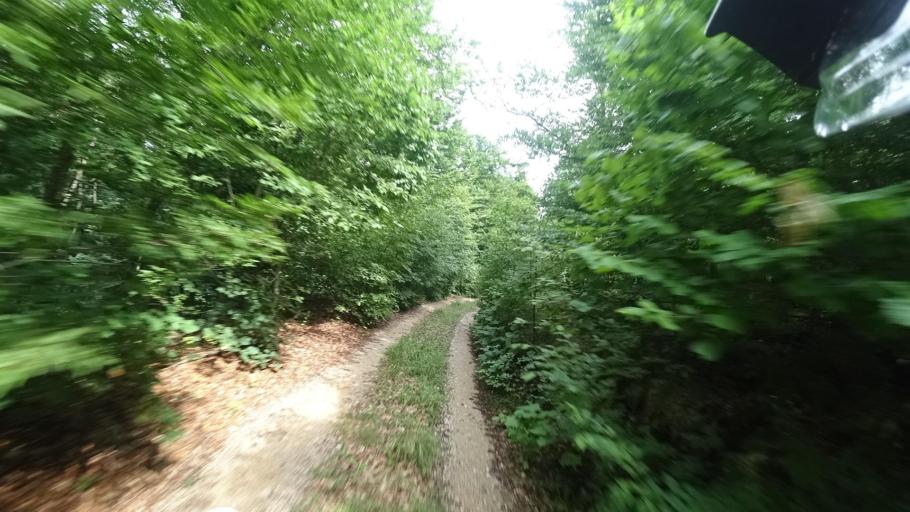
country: BA
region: Federation of Bosnia and Herzegovina
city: Bihac
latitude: 44.6522
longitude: 15.7615
